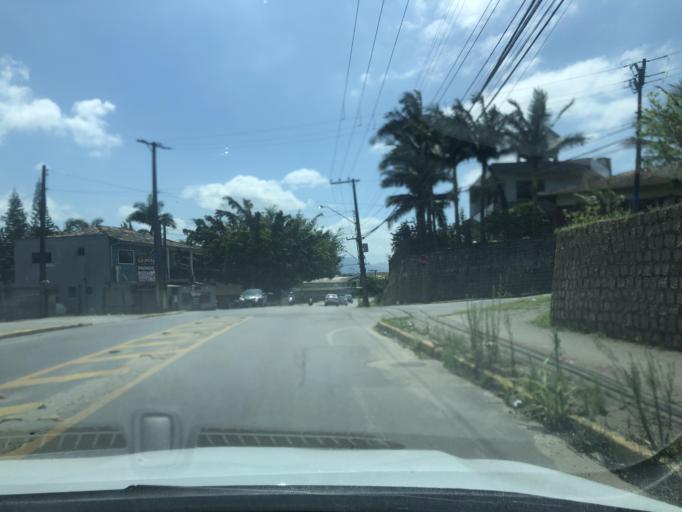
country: BR
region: Santa Catarina
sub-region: Joinville
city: Joinville
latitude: -26.3313
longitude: -48.8282
